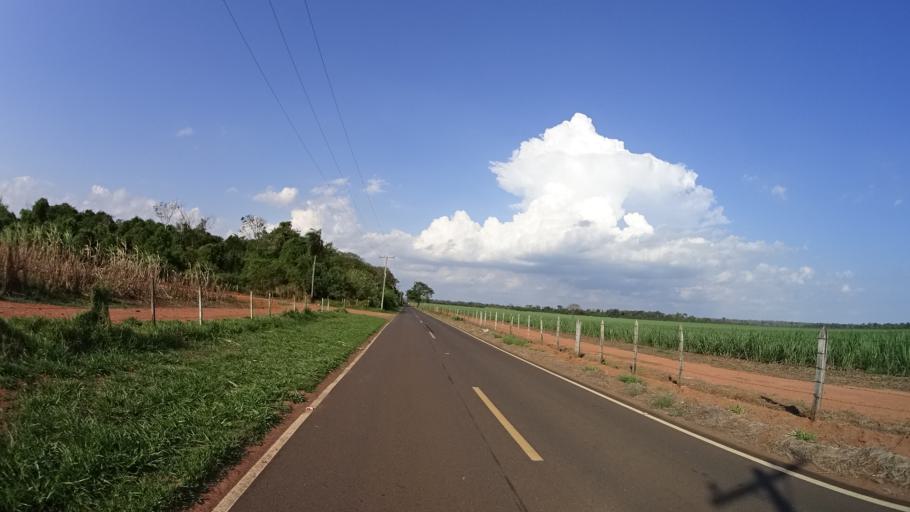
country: BR
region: Sao Paulo
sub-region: Urupes
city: Urupes
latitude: -21.3877
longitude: -49.4991
